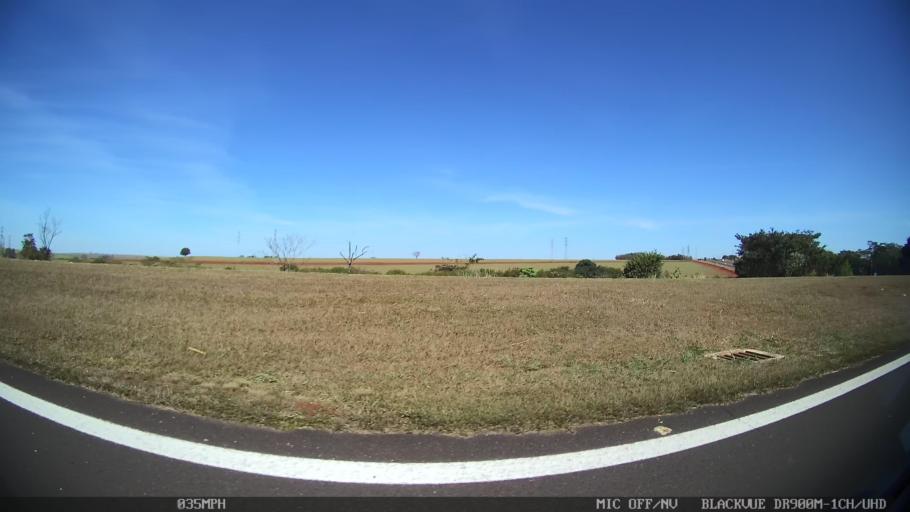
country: BR
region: Sao Paulo
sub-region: Sao Joaquim Da Barra
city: Sao Joaquim da Barra
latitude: -20.5254
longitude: -47.8410
